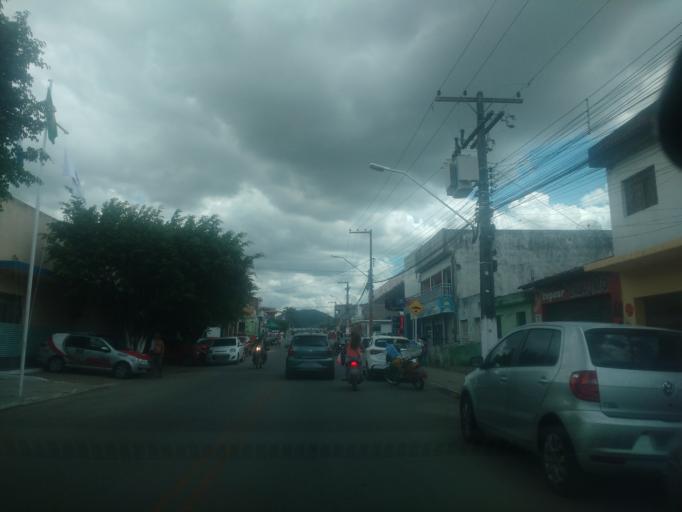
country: BR
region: Alagoas
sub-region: Uniao Dos Palmares
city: Uniao dos Palmares
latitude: -9.1566
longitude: -36.0275
